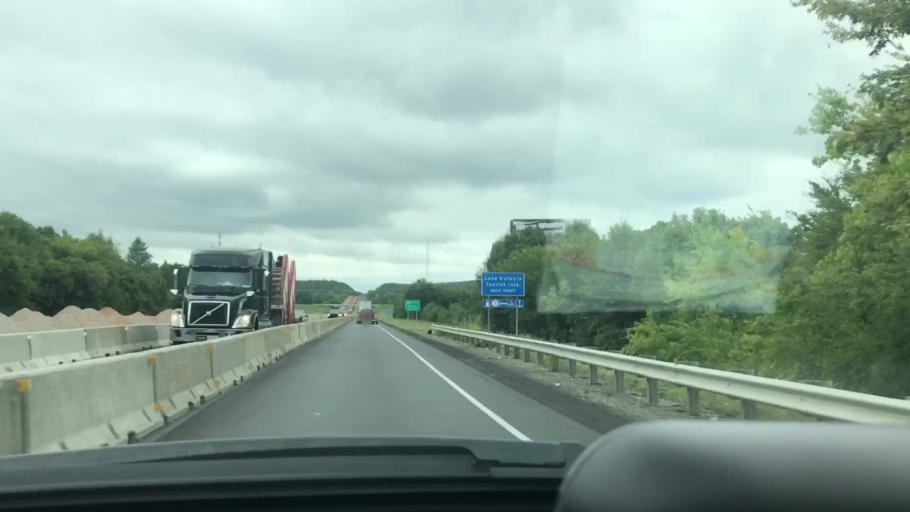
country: US
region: Oklahoma
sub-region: McIntosh County
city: Eufaula
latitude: 35.2560
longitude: -95.5868
